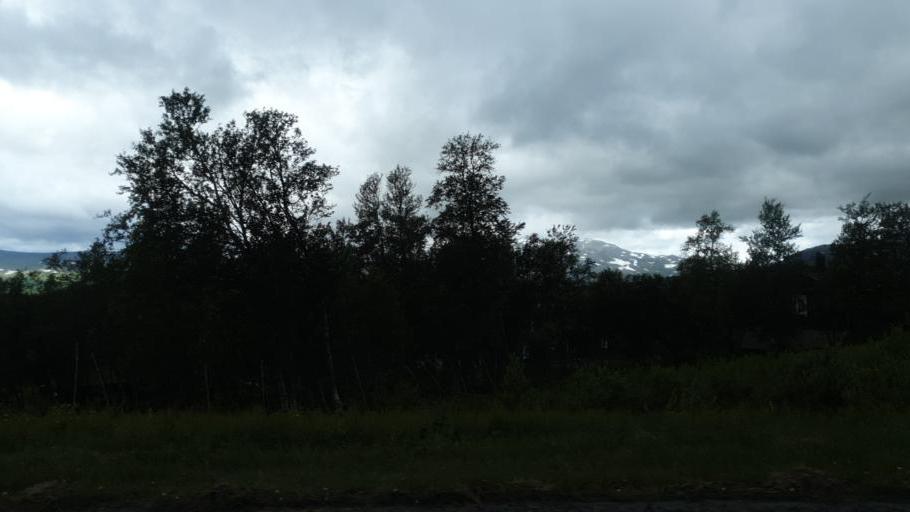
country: NO
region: Oppland
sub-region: Vestre Slidre
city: Slidre
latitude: 61.2598
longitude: 8.8745
